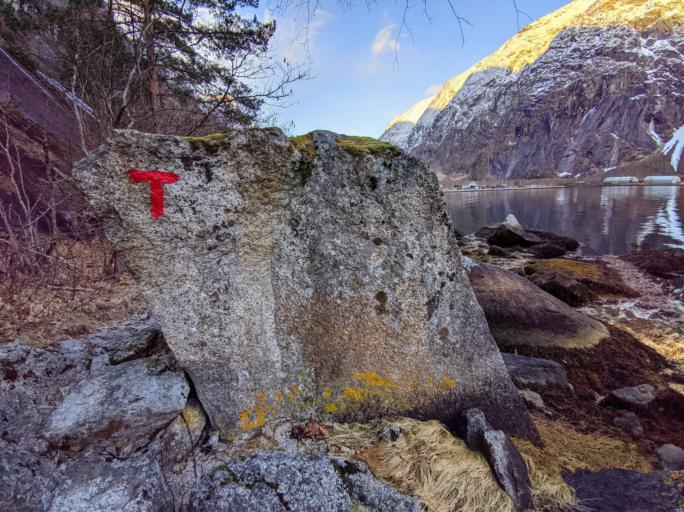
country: NO
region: Hordaland
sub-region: Eidfjord
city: Eidfjord
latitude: 60.4996
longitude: 7.1311
